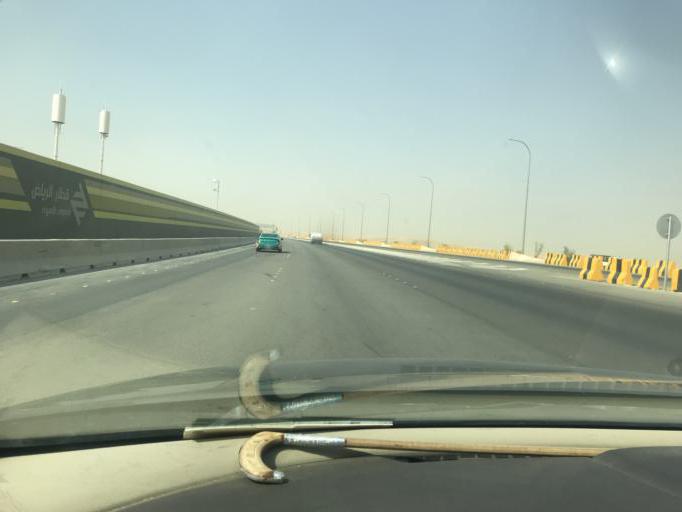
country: SA
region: Ar Riyad
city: Riyadh
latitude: 24.9001
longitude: 46.7019
